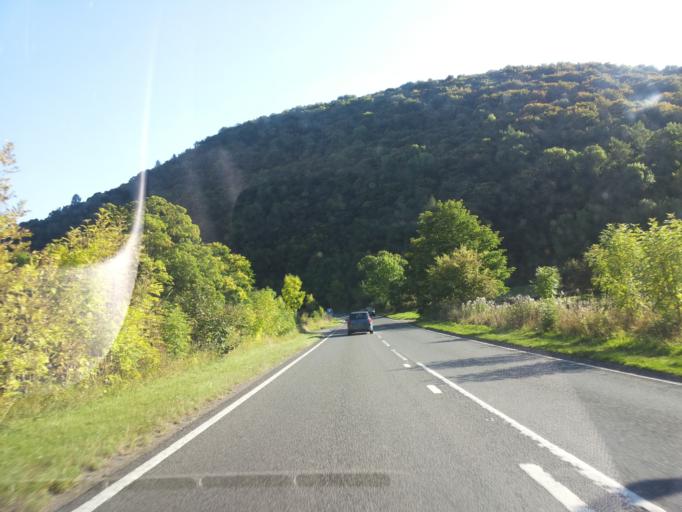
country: GB
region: England
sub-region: Derbyshire
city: Tideswell
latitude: 53.2314
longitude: -1.7450
